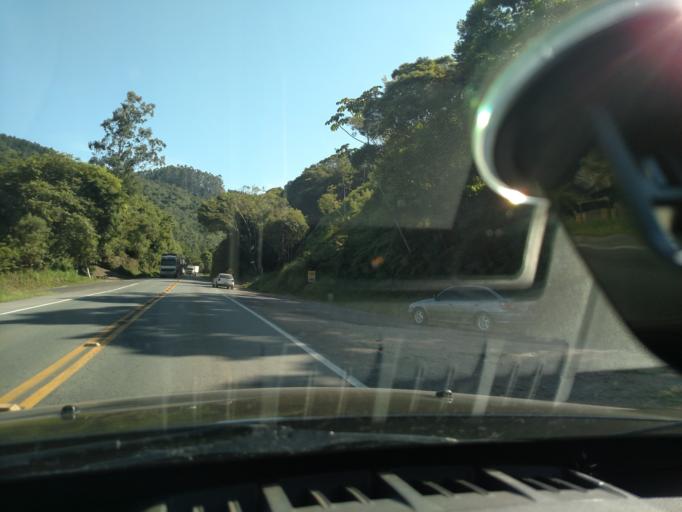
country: BR
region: Santa Catarina
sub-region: Ibirama
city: Ibirama
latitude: -27.0797
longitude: -49.4994
